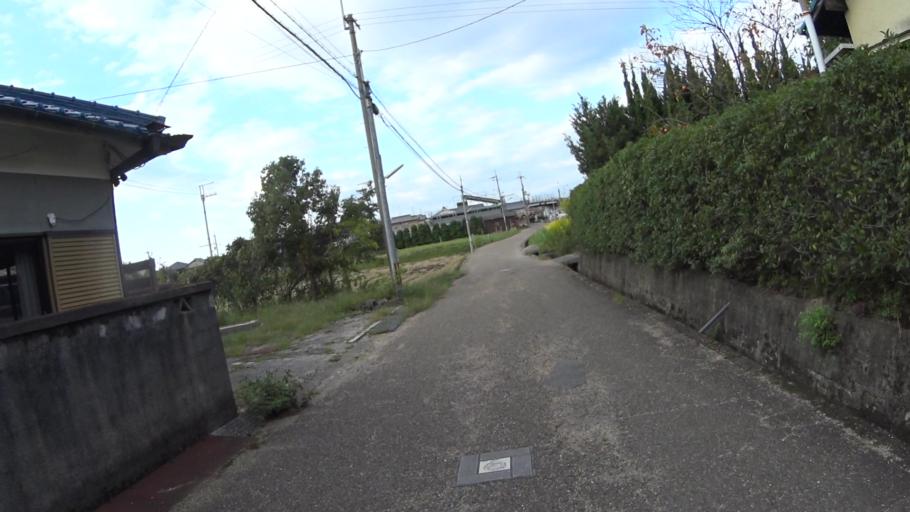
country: JP
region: Nara
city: Tenri
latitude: 34.5417
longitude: 135.8415
